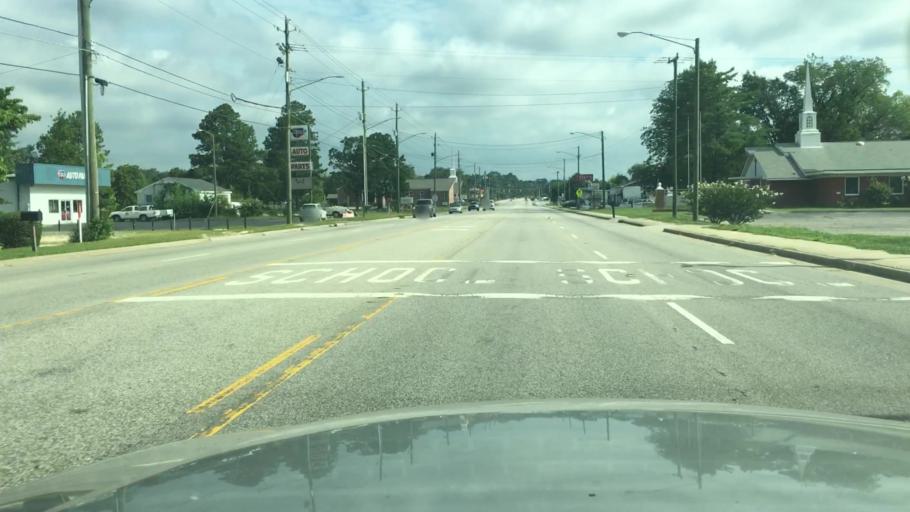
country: US
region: North Carolina
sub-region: Cumberland County
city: Hope Mills
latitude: 35.0005
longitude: -78.9673
